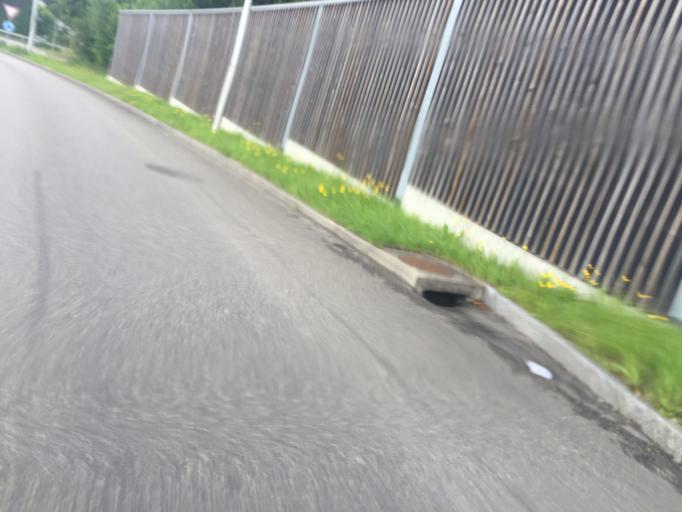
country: CH
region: Bern
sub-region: Bern-Mittelland District
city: Koniz
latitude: 46.9260
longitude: 7.3806
